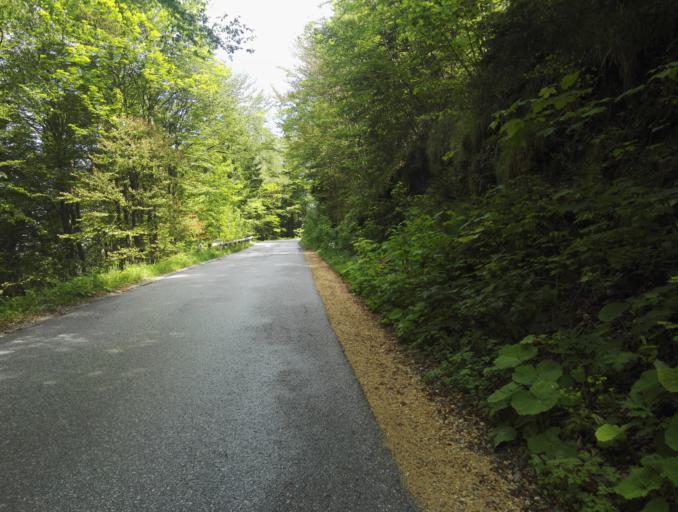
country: AT
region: Styria
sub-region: Politischer Bezirk Graz-Umgebung
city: Sankt Radegund bei Graz
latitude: 47.2087
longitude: 15.4609
